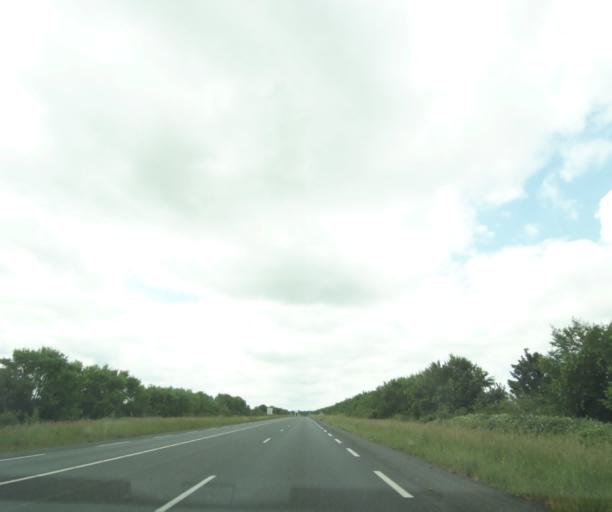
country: FR
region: Poitou-Charentes
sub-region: Departement des Deux-Sevres
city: Saint-Varent
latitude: 46.8820
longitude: -0.1953
